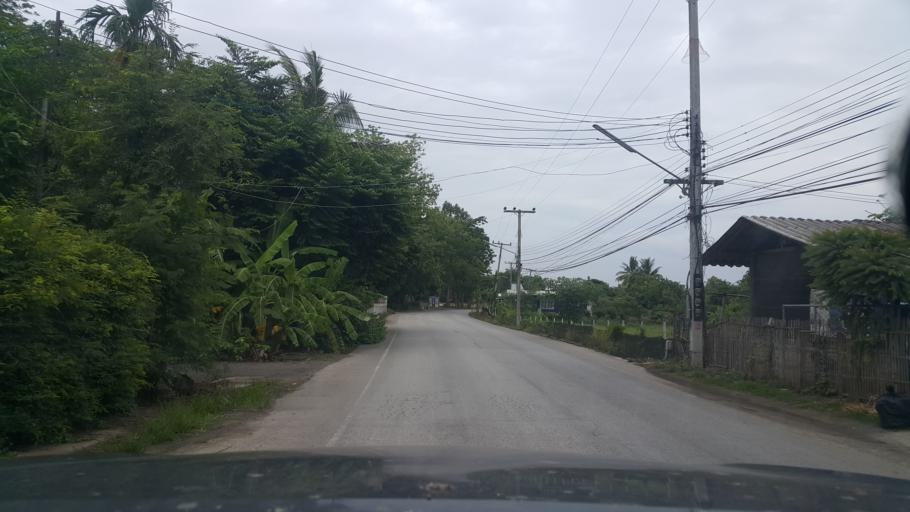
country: TH
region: Chiang Mai
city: San Pa Tong
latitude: 18.6561
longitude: 98.8373
